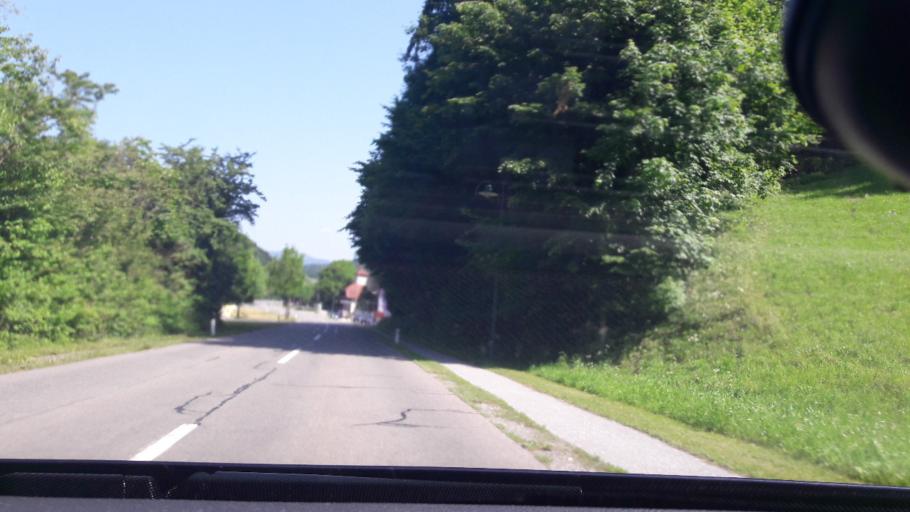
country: AT
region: Styria
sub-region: Politischer Bezirk Voitsberg
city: Sodingberg
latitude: 47.1056
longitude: 15.1734
